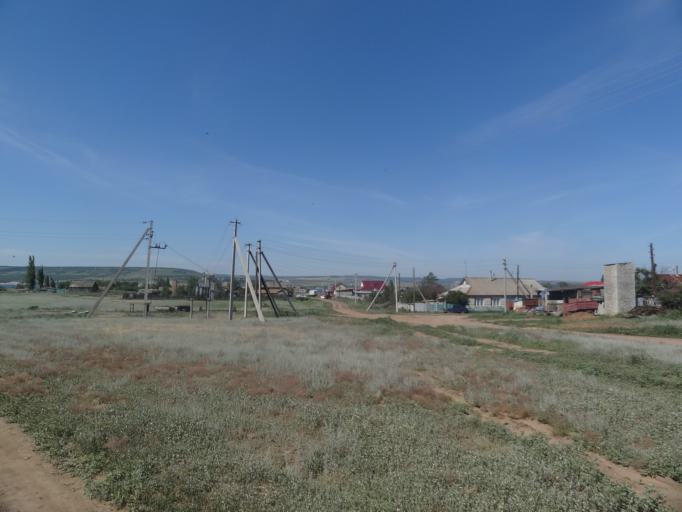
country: RU
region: Saratov
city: Krasnoarmeysk
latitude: 51.0823
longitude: 45.9580
